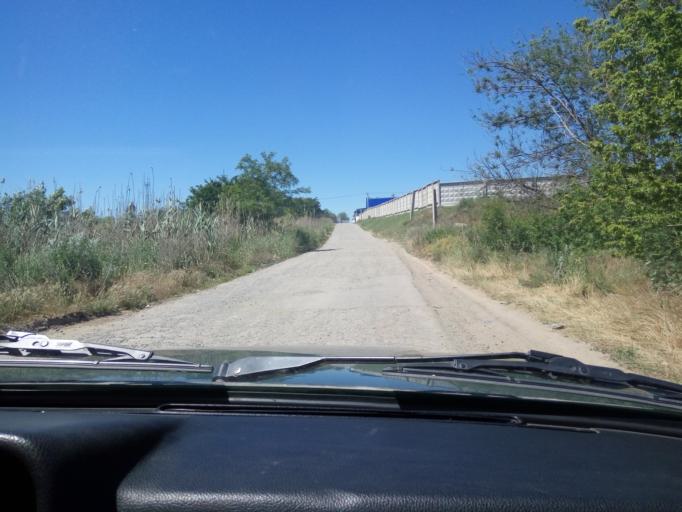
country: RU
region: Rostov
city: Bataysk
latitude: 47.0834
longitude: 39.7482
